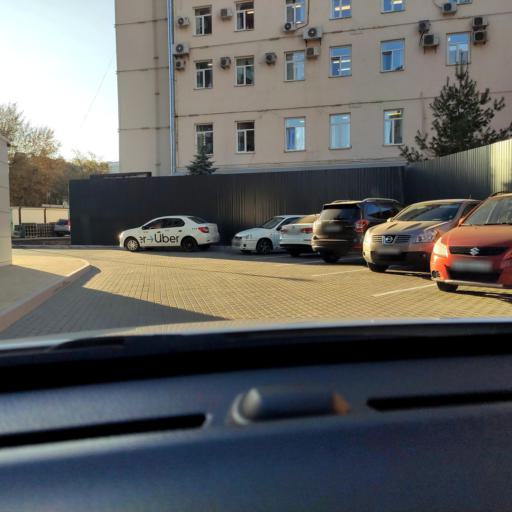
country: RU
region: Voronezj
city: Voronezh
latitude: 51.6538
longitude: 39.1944
